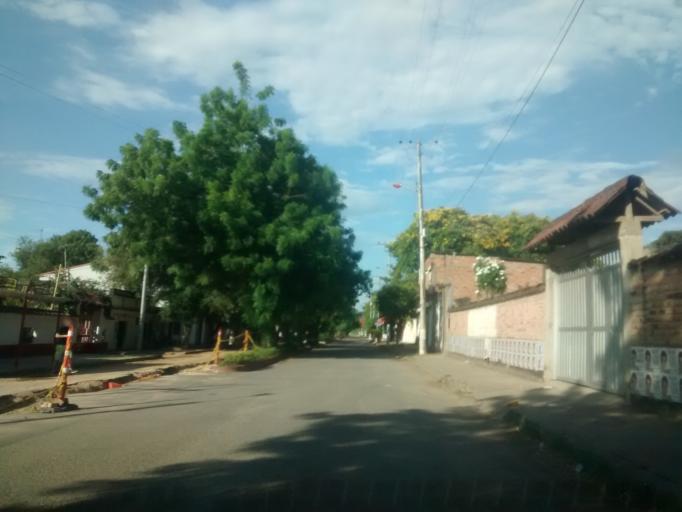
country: CO
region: Cundinamarca
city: Ricaurte
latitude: 4.2757
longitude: -74.7732
